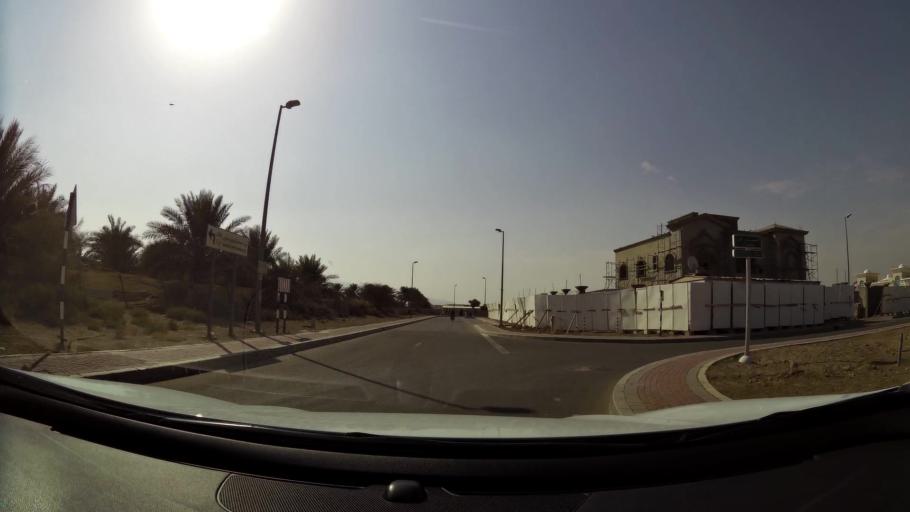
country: AE
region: Abu Dhabi
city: Al Ain
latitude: 24.0896
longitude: 55.9078
